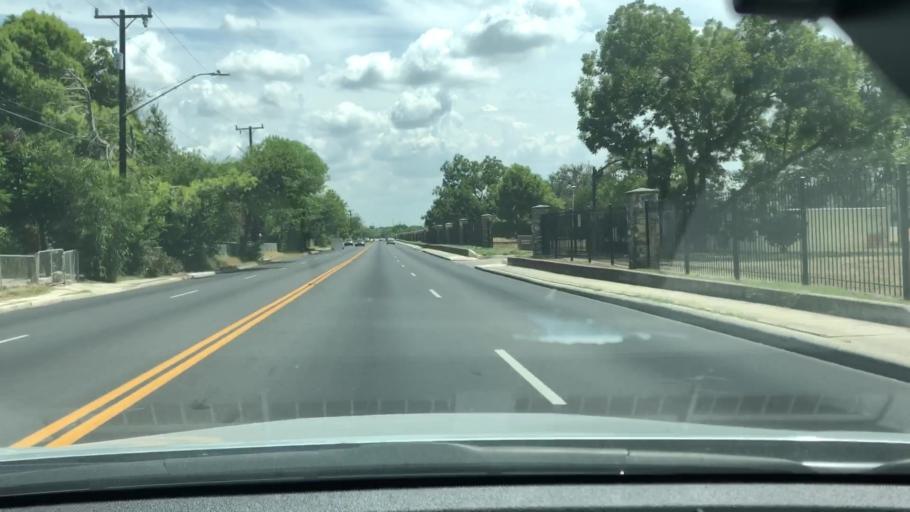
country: US
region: Texas
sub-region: Bexar County
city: Terrell Hills
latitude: 29.4848
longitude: -98.4263
